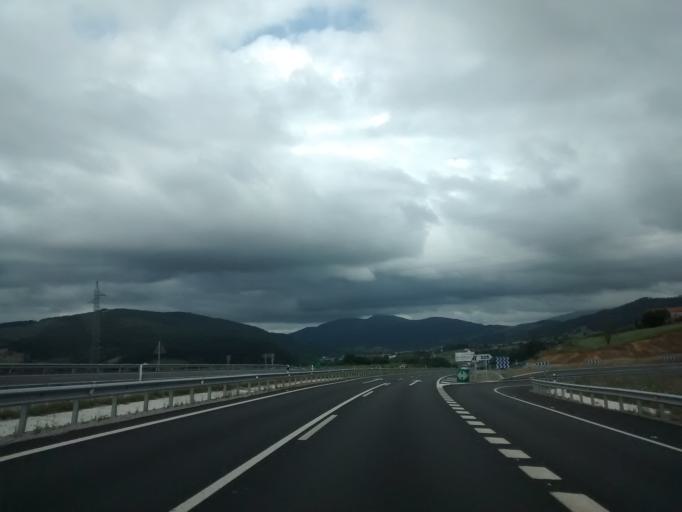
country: ES
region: Cantabria
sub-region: Provincia de Cantabria
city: Polanco
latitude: 43.3440
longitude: -3.9940
